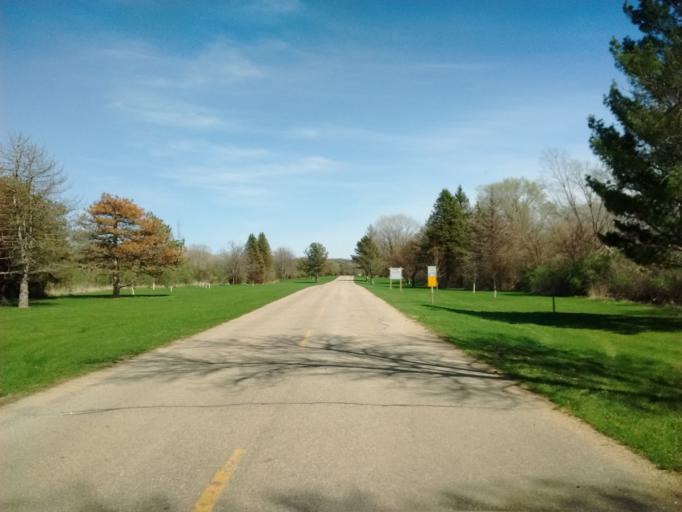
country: US
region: Iowa
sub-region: Plymouth County
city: Kingsley
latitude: 42.4514
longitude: -95.8055
